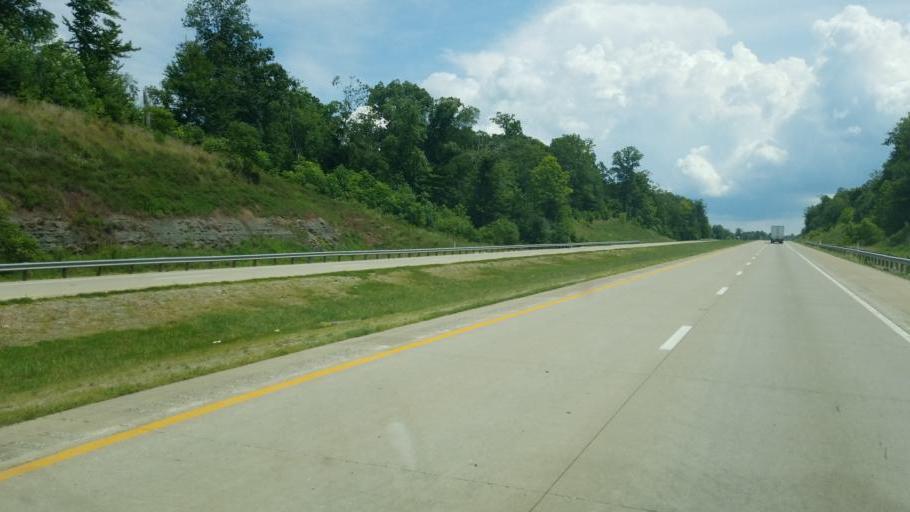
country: US
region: West Virginia
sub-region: Putnam County
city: Eleanor
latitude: 38.5435
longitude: -81.9699
